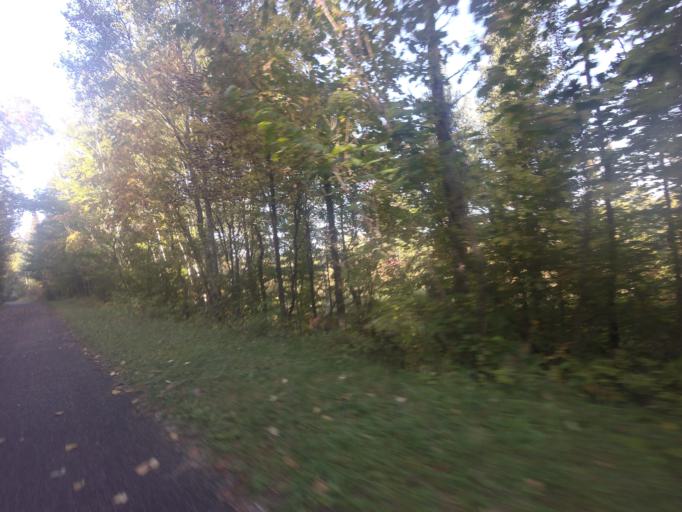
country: CA
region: Quebec
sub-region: Laurentides
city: Mont-Laurier
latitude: 46.5280
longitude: -75.3097
